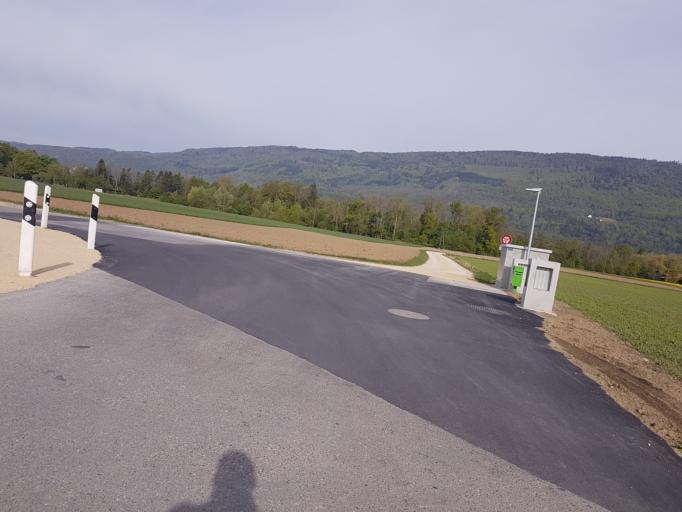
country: CH
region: Bern
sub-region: Biel/Bienne District
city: Bellmund
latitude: 47.1106
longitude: 7.2249
